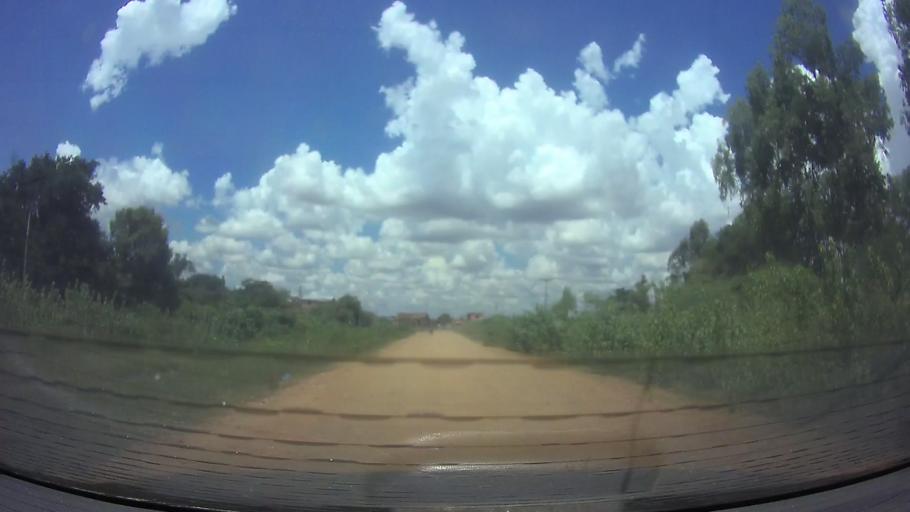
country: PY
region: Presidente Hayes
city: Nanawa
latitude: -25.2541
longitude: -57.6417
